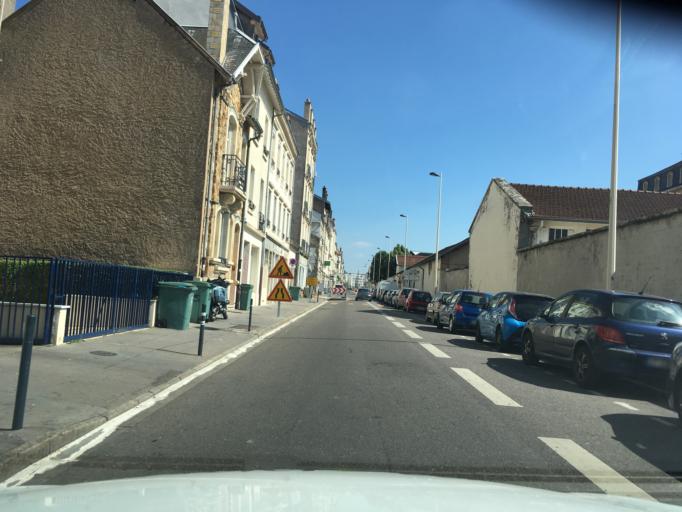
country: FR
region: Lorraine
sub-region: Departement de Meurthe-et-Moselle
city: Nancy
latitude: 48.6770
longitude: 6.1690
